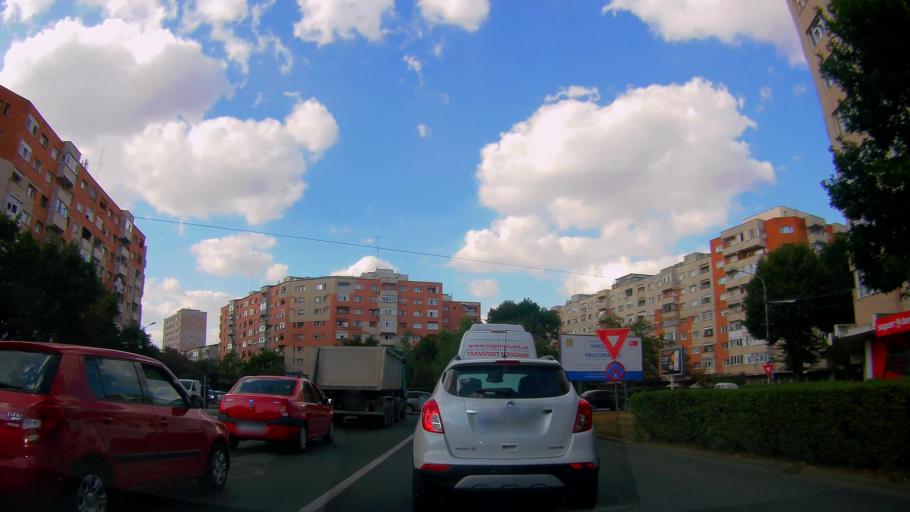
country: RO
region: Satu Mare
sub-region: Municipiul Satu Mare
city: Satu Mare
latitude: 47.7792
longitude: 22.8830
